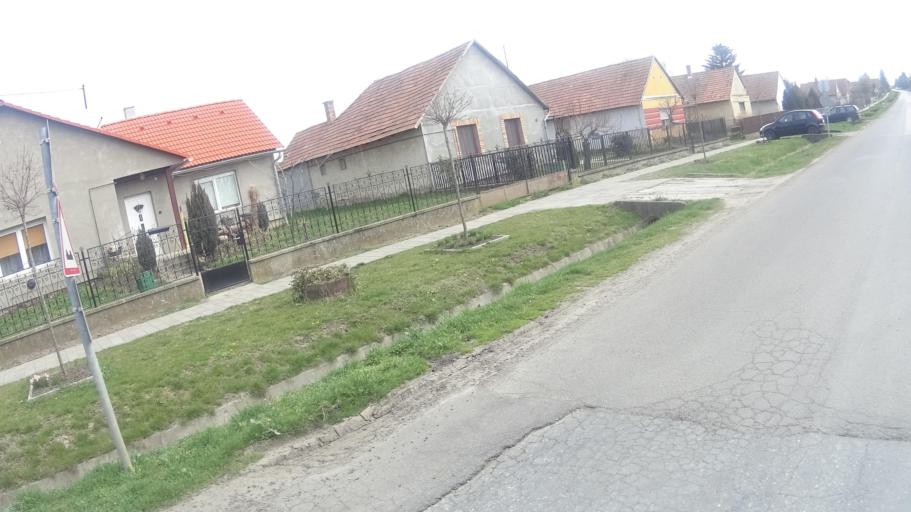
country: HU
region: Fejer
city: Sarosd
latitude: 46.9774
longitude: 18.6443
